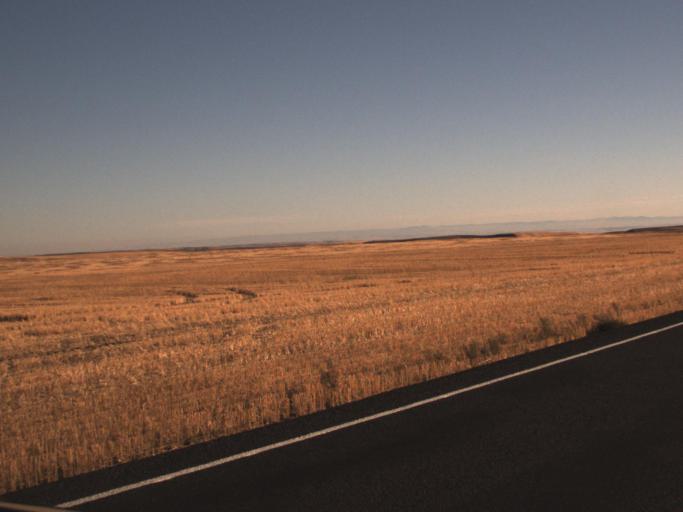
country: US
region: Washington
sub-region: Adams County
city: Ritzville
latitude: 46.8599
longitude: -118.3361
